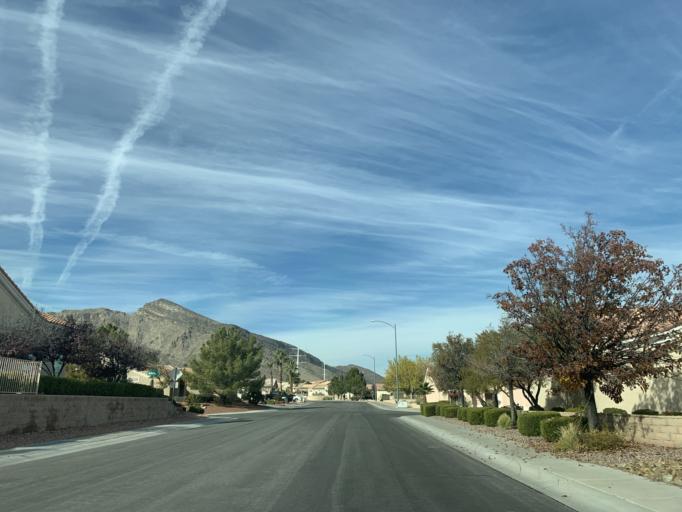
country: US
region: Nevada
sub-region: Clark County
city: Summerlin South
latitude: 36.2150
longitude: -115.3262
